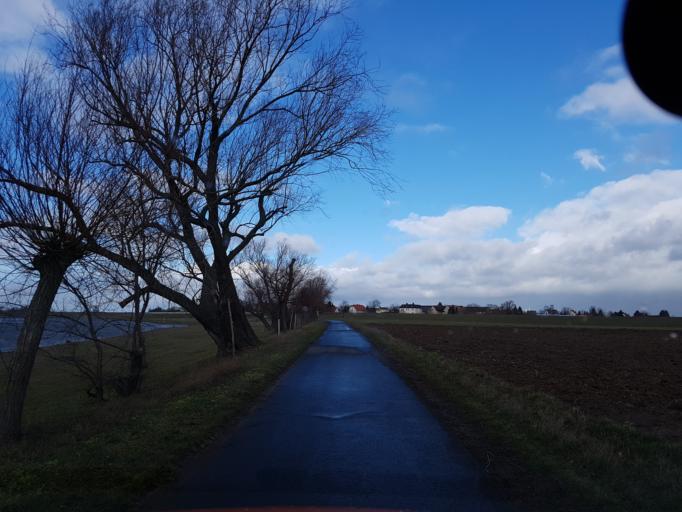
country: DE
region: Saxony
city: Belgern
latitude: 51.4892
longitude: 13.1874
